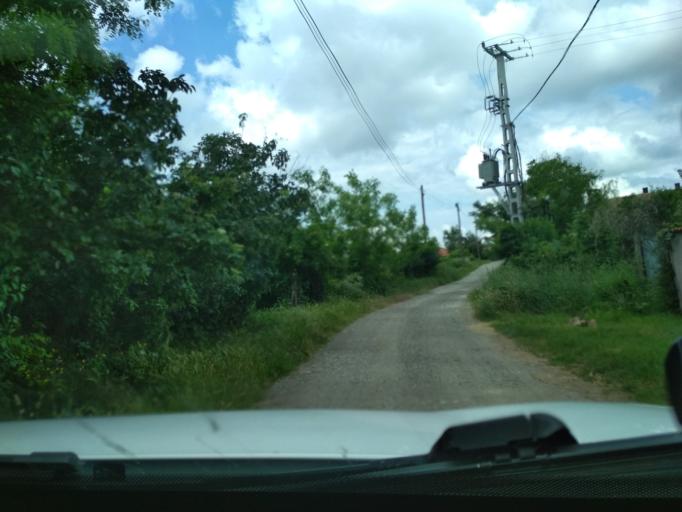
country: HU
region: Jasz-Nagykun-Szolnok
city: Tiszafured
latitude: 47.6116
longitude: 20.7416
